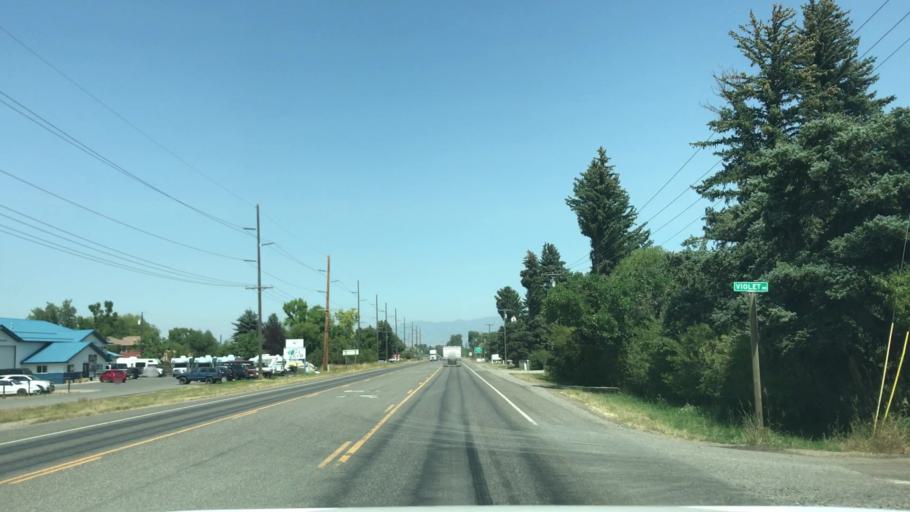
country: US
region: Montana
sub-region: Gallatin County
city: Four Corners
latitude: 45.6529
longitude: -111.1895
